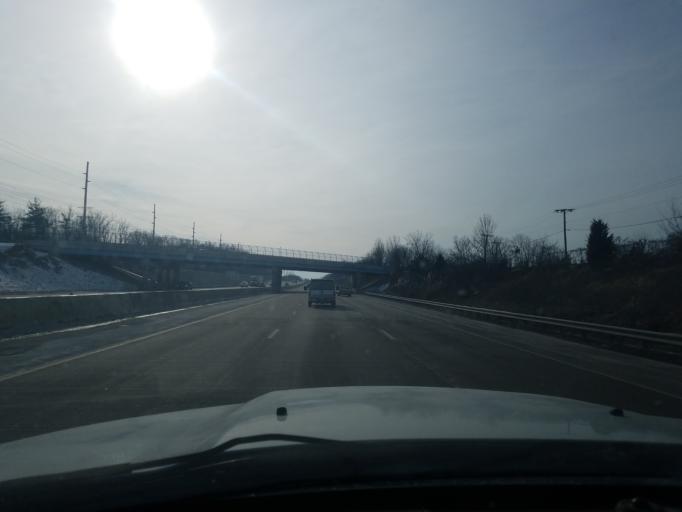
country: US
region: Indiana
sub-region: Allen County
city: Fort Wayne
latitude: 41.0608
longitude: -85.2388
